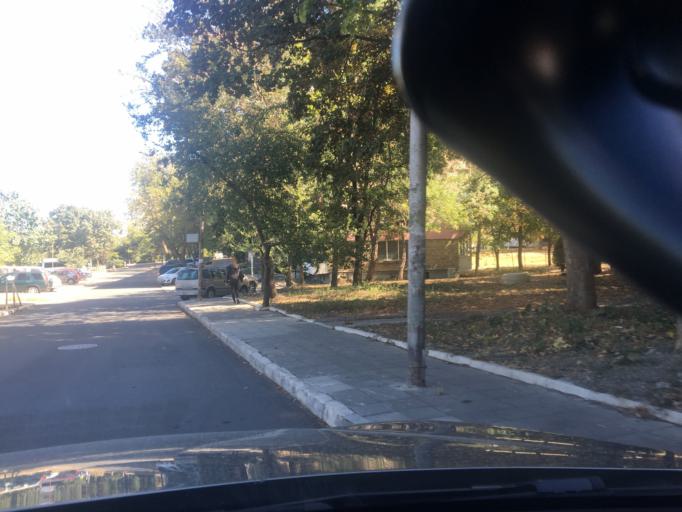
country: BG
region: Burgas
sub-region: Obshtina Burgas
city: Burgas
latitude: 42.5112
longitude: 27.4724
